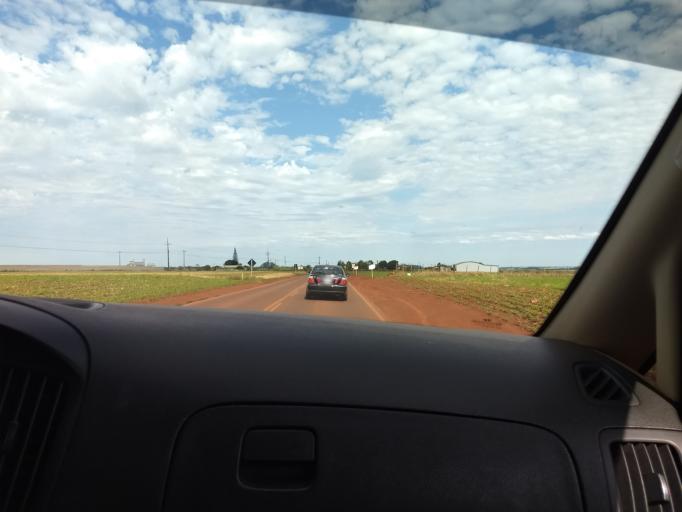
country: PY
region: Alto Parana
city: Santa Rita
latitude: -25.8025
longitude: -55.0636
